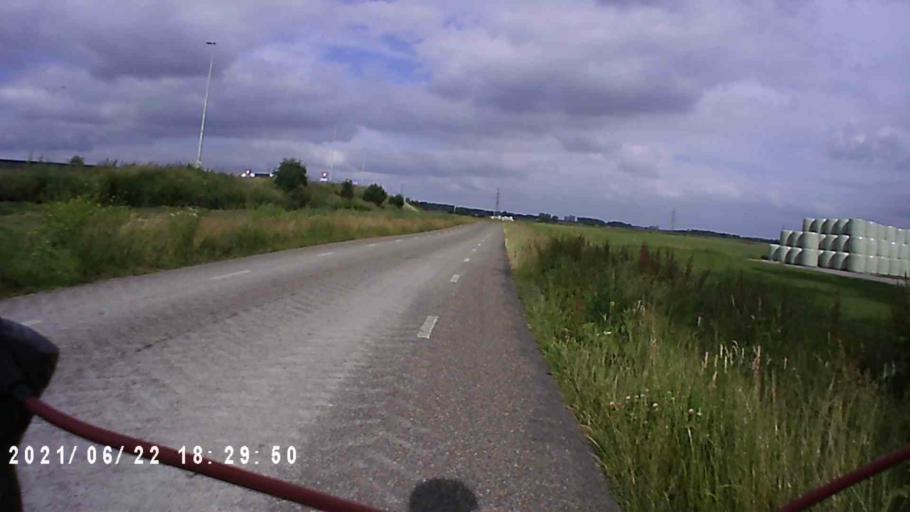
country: NL
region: Groningen
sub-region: Gemeente Zuidhorn
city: Aduard
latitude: 53.2015
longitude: 6.4717
